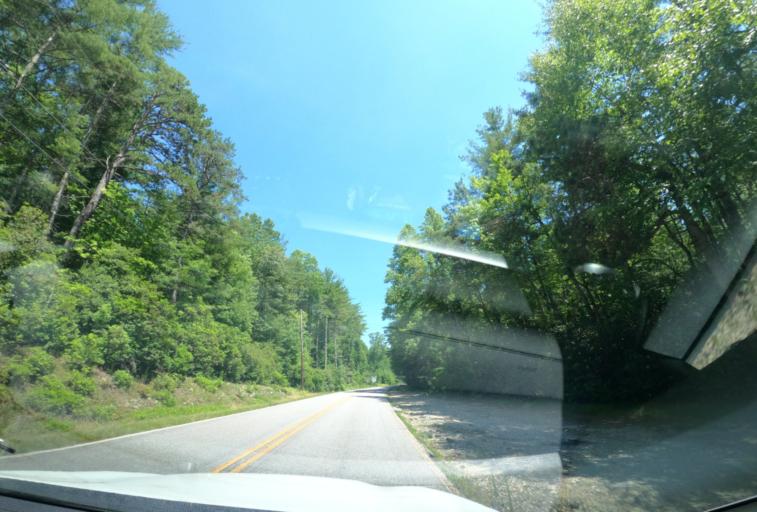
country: US
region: North Carolina
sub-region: Transylvania County
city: Brevard
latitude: 35.1832
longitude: -82.6430
